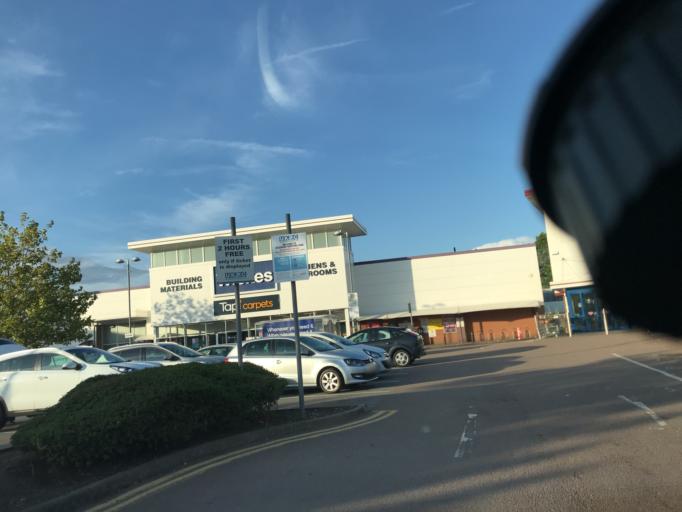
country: GB
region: England
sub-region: Buckinghamshire
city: Aylesbury
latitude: 51.8201
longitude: -0.8088
